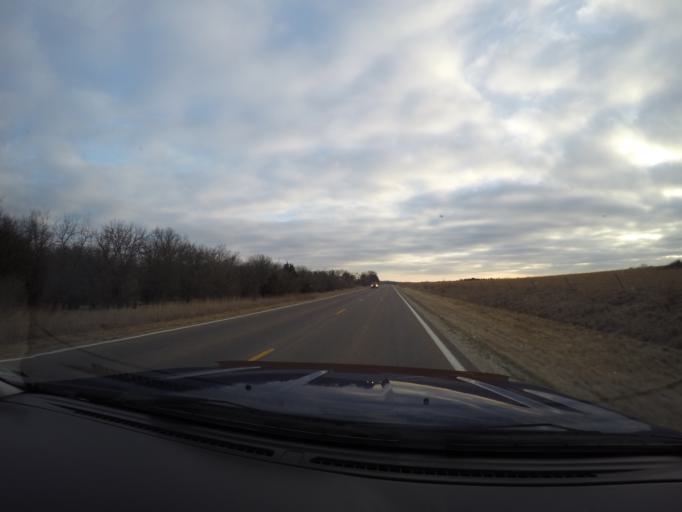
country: US
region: Kansas
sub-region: Morris County
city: Council Grove
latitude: 38.7459
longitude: -96.5012
